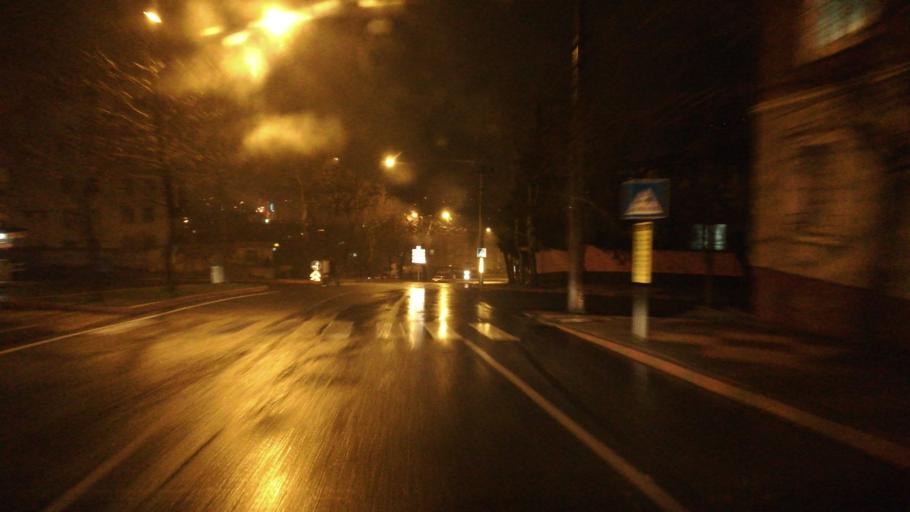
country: TR
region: Kahramanmaras
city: Kahramanmaras
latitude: 37.5879
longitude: 36.9394
